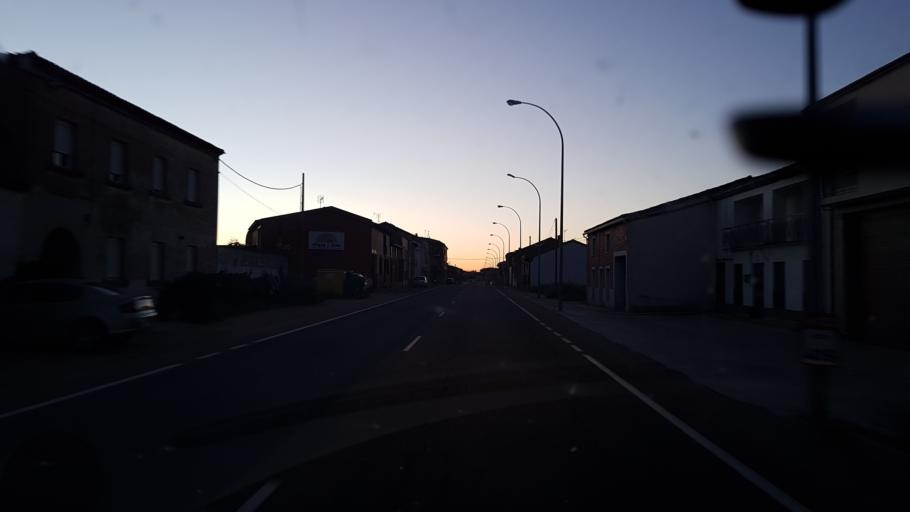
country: ES
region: Castille and Leon
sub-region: Provincia de Zamora
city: Morales de Toro
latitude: 41.5346
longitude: -5.3113
